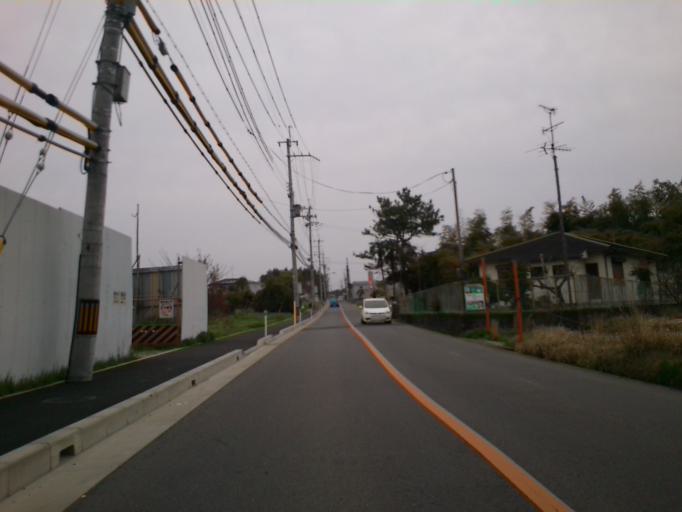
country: JP
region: Kyoto
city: Tanabe
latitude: 34.8431
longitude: 135.7391
